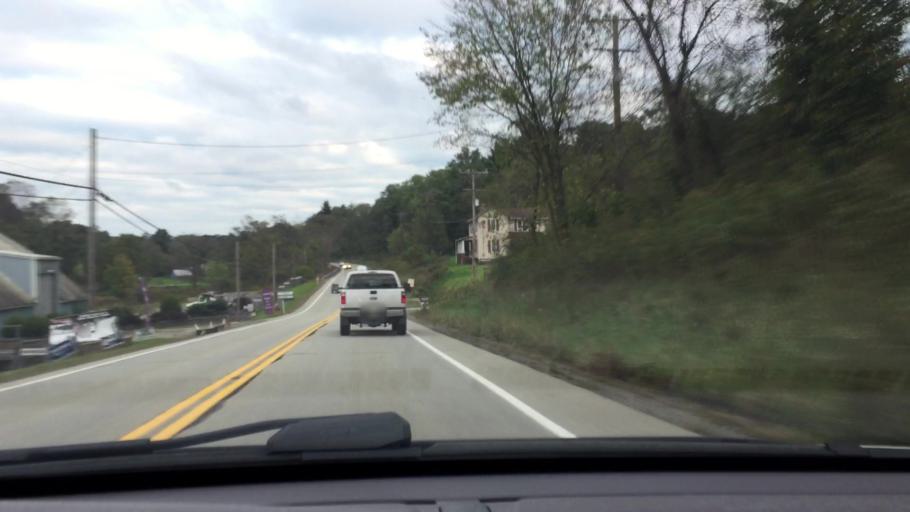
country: US
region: Pennsylvania
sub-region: Washington County
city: Canonsburg
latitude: 40.2213
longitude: -80.1554
